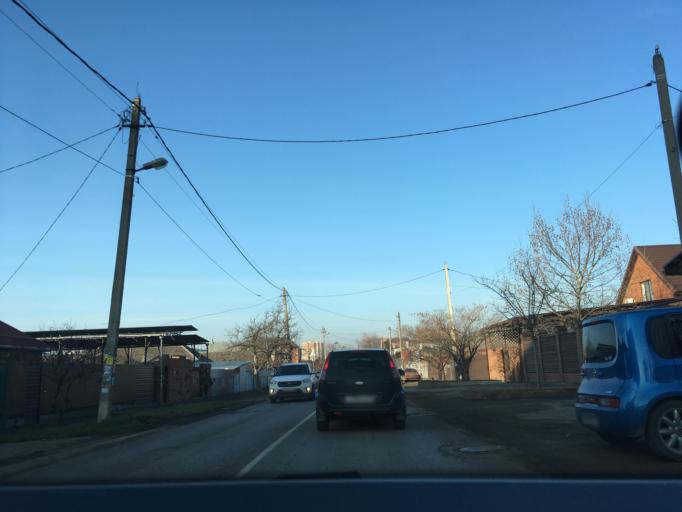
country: RU
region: Krasnodarskiy
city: Krasnodar
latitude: 45.0766
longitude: 39.0209
